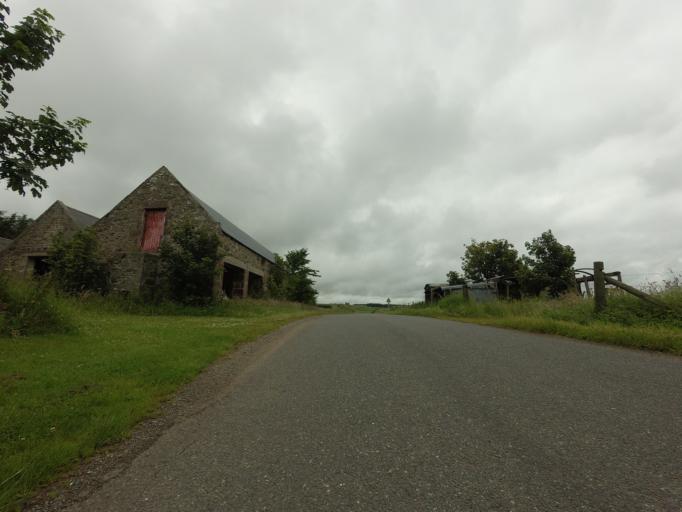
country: GB
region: Scotland
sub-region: Aberdeenshire
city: Turriff
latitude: 57.5428
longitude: -2.2734
